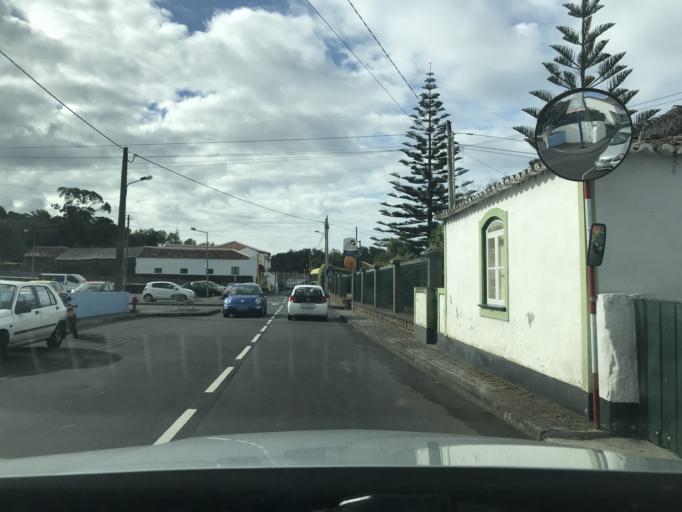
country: PT
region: Azores
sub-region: Angra do Heroismo
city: Angra do Heroismo
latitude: 38.6739
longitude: -27.2485
